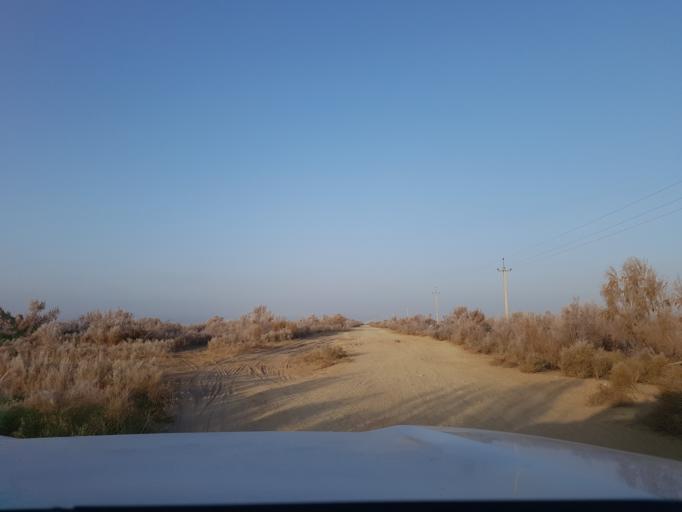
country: TM
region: Dasoguz
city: Koeneuergench
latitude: 41.8499
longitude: 58.3137
